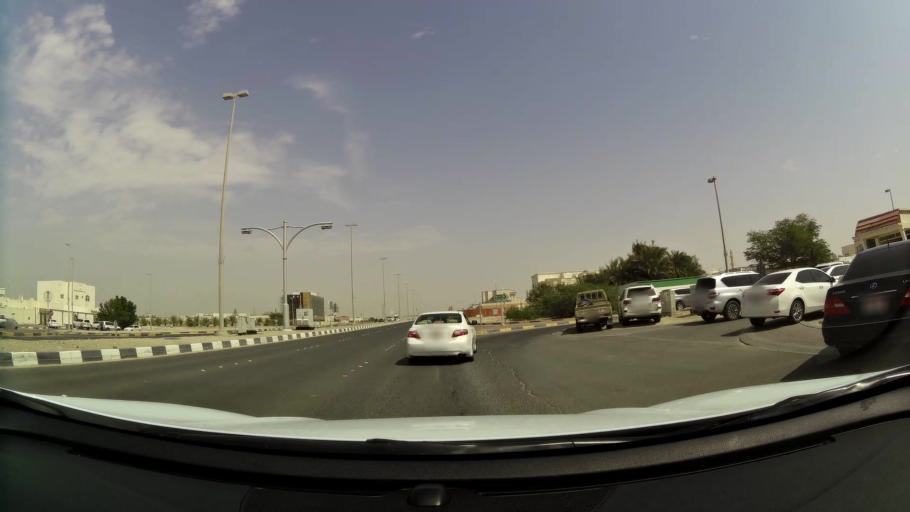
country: AE
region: Abu Dhabi
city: Abu Dhabi
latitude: 24.3033
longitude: 54.6363
